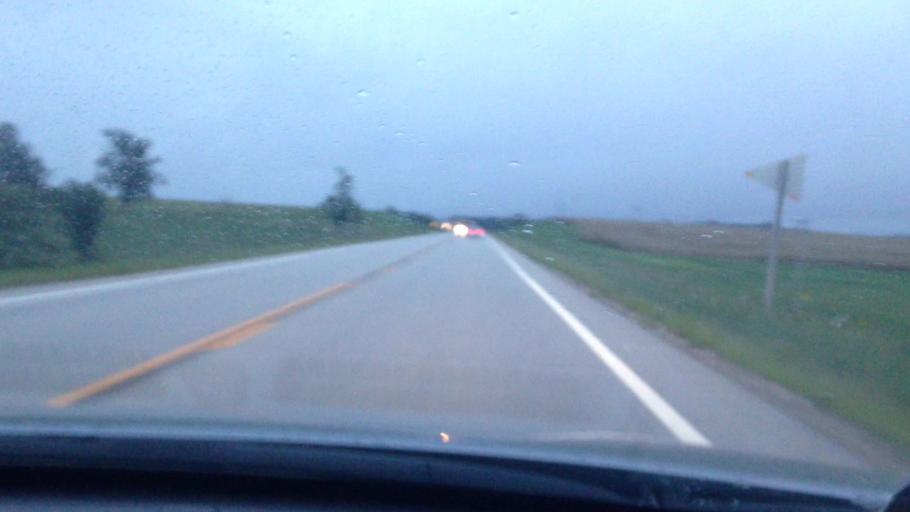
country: US
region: Kansas
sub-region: Brown County
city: Horton
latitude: 39.6675
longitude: -95.4865
